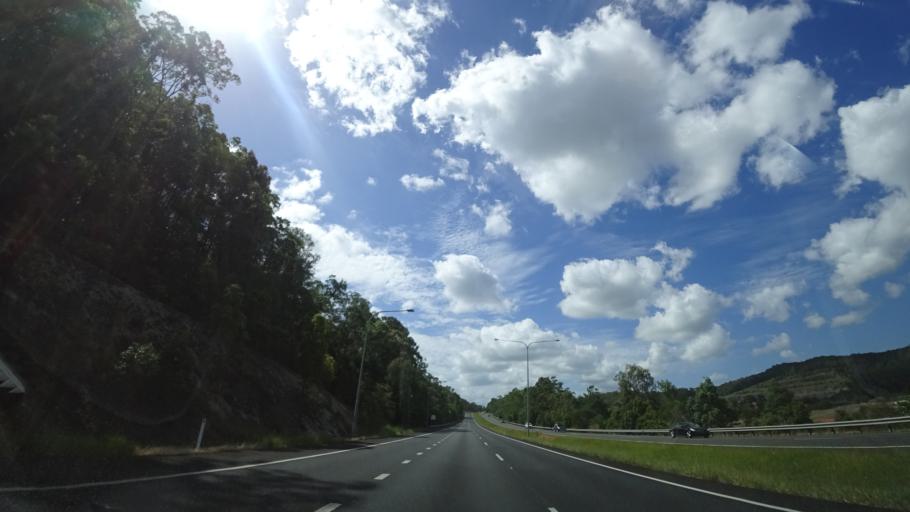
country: AU
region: Queensland
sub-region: Sunshine Coast
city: Twin Waters
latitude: -26.6133
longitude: 152.9780
